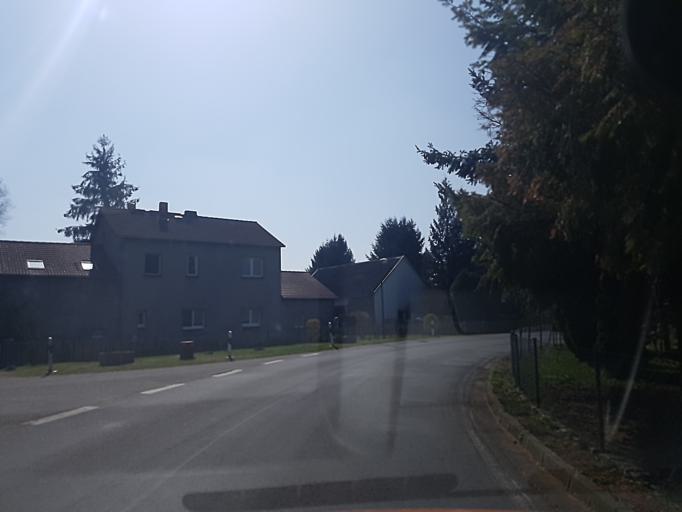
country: DE
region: Saxony
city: Gross Duben
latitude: 51.6759
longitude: 14.5380
